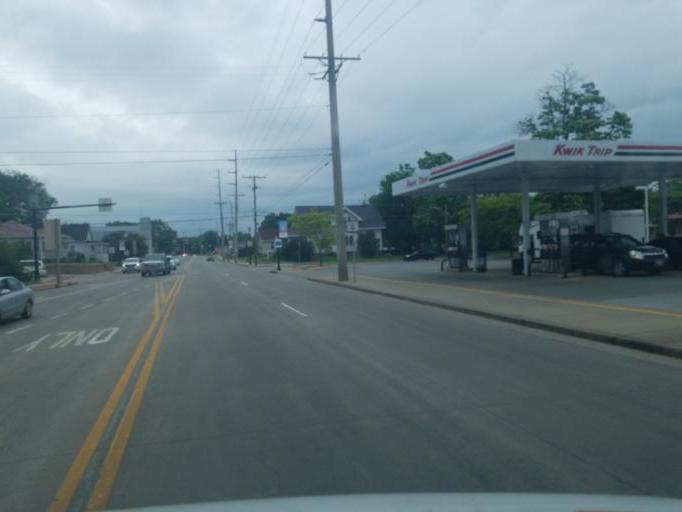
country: US
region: Wisconsin
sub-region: Juneau County
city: Mauston
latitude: 43.7957
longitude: -90.0720
